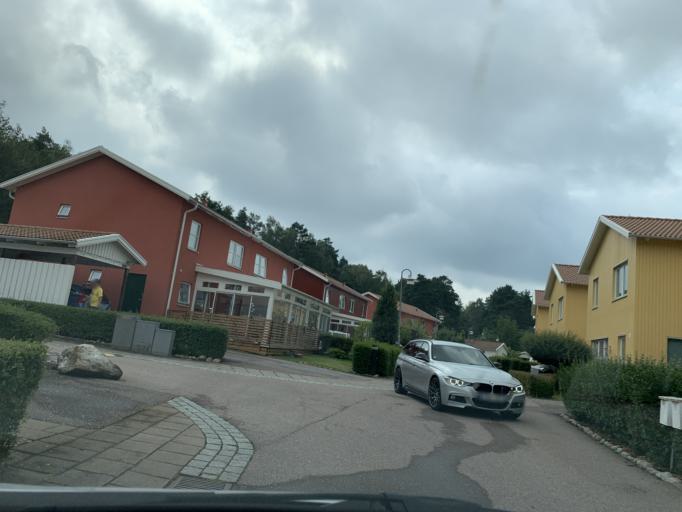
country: SE
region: Vaestra Goetaland
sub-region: Goteborg
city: Eriksbo
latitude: 57.7441
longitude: 12.0350
